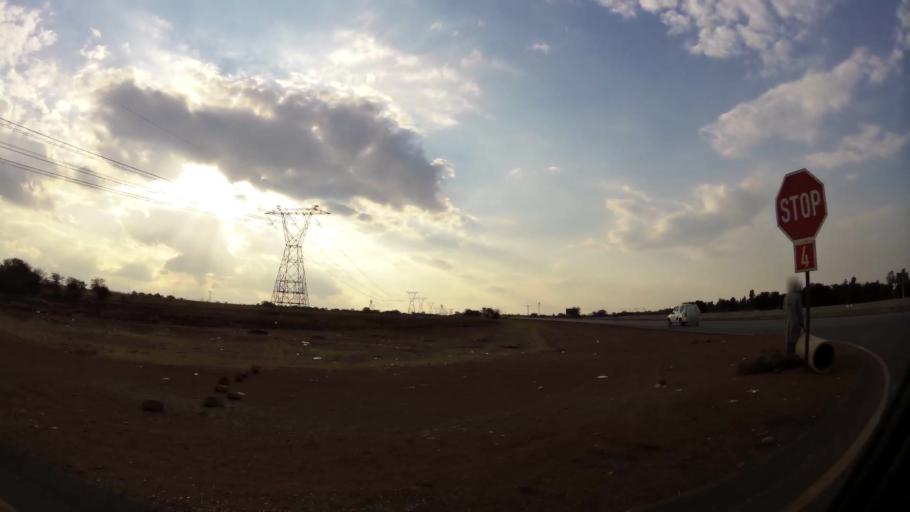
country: ZA
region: Gauteng
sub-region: Sedibeng District Municipality
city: Vereeniging
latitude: -26.6503
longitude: 27.8774
